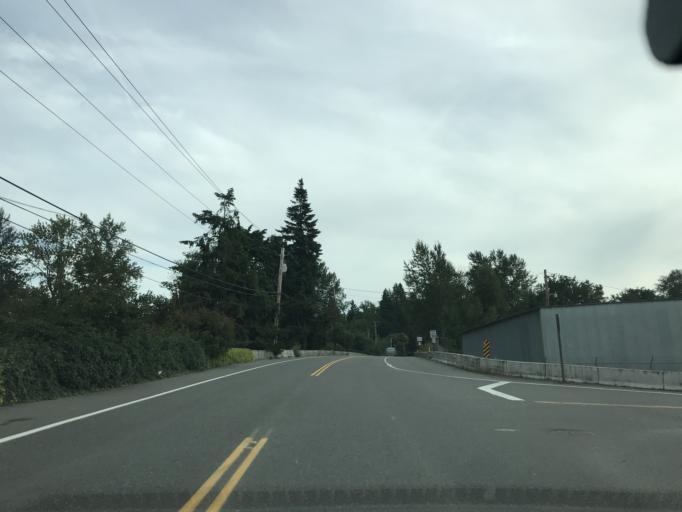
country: US
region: Washington
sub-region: King County
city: Fall City
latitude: 47.5656
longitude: -121.8883
